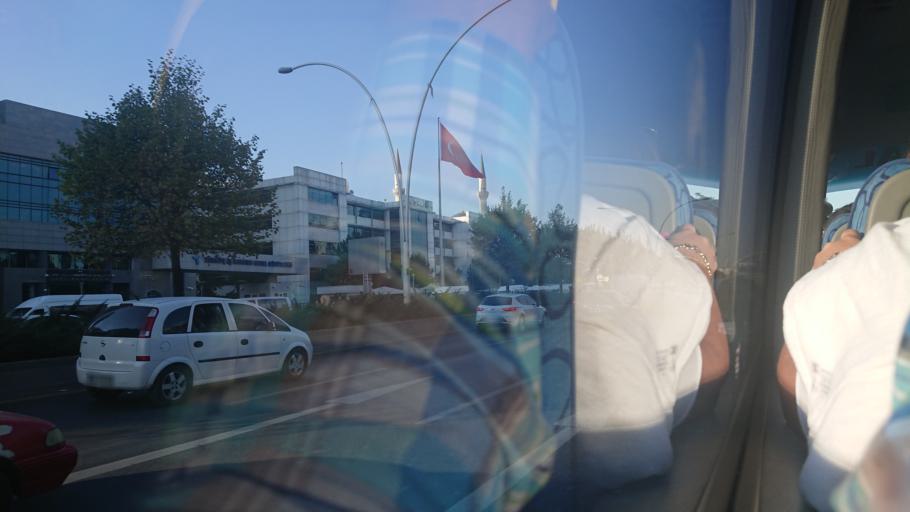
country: TR
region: Ankara
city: Ankara
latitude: 39.9396
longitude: 32.8258
